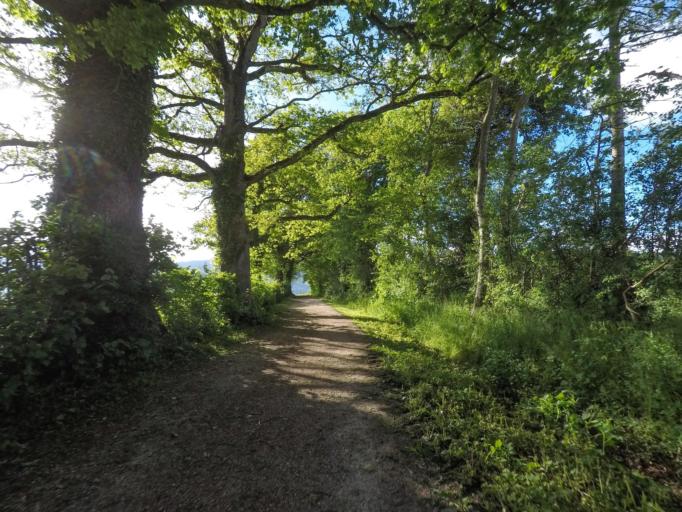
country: FR
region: Rhone-Alpes
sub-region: Departement de l'Ain
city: Segny
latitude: 46.2694
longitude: 6.0678
